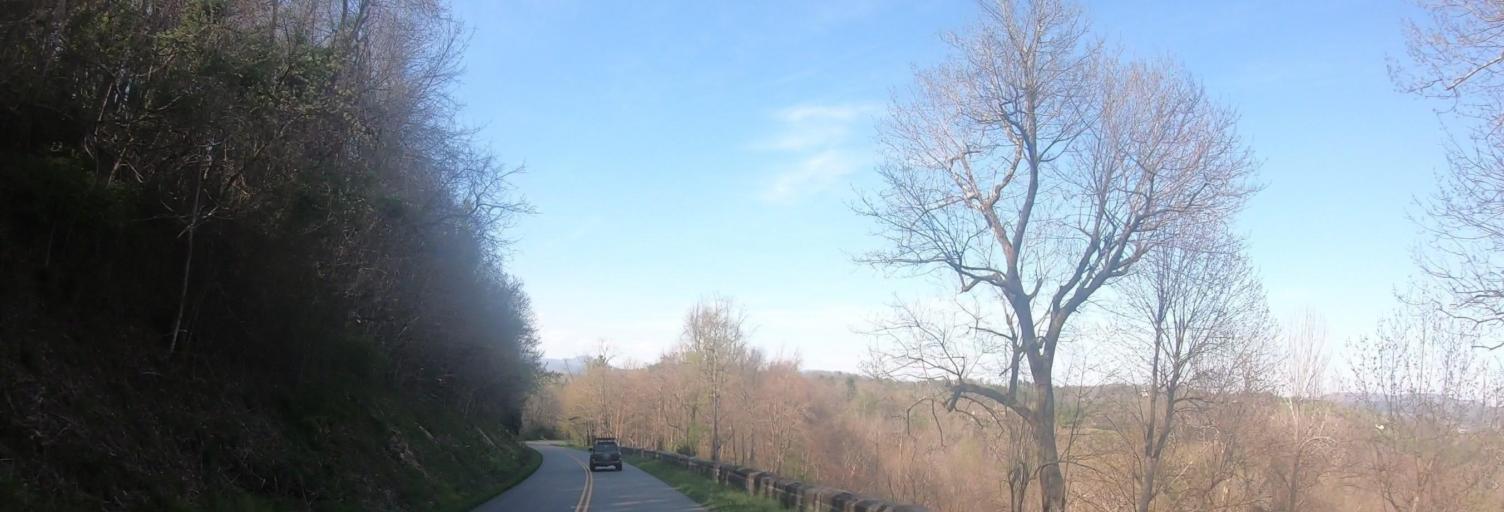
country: US
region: North Carolina
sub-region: Watauga County
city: Boone
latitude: 36.2117
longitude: -81.6005
